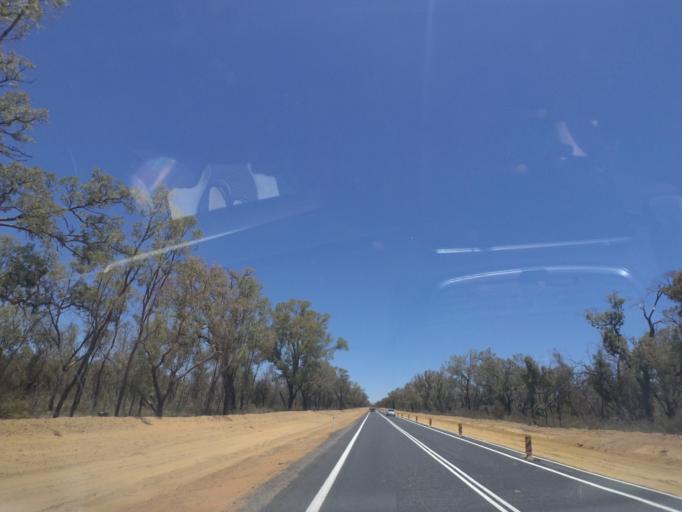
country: AU
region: New South Wales
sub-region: Warrumbungle Shire
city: Coonabarabran
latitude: -30.9321
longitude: 149.4281
